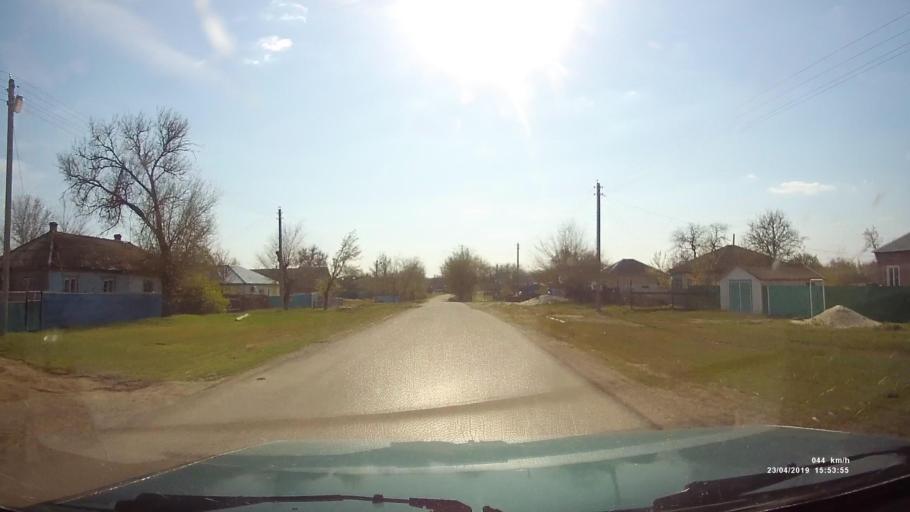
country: RU
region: Rostov
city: Remontnoye
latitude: 46.5373
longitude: 43.1324
